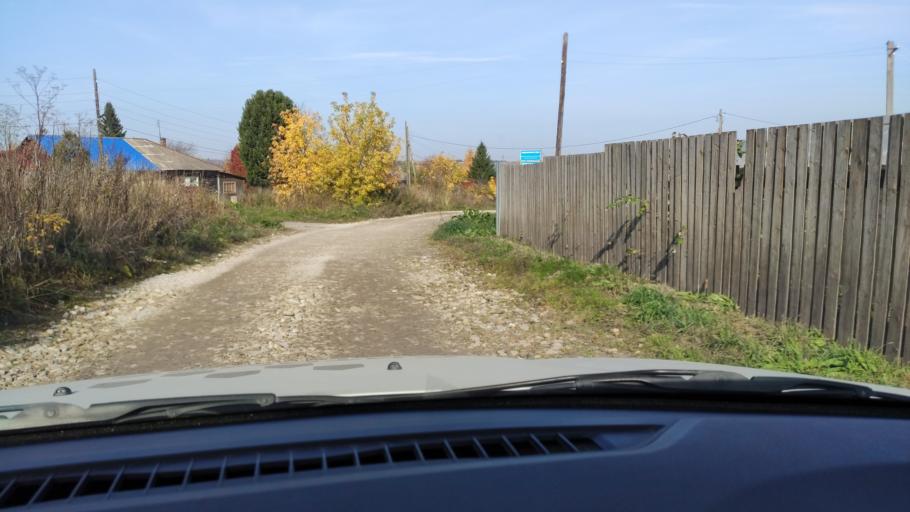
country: RU
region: Perm
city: Sylva
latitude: 58.0457
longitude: 56.7378
